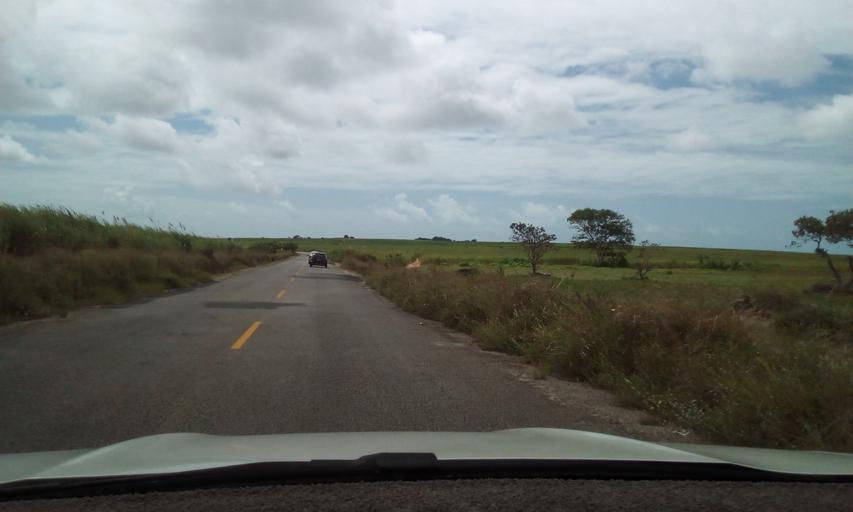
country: BR
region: Paraiba
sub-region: Rio Tinto
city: Rio Tinto
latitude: -6.7663
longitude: -35.0041
